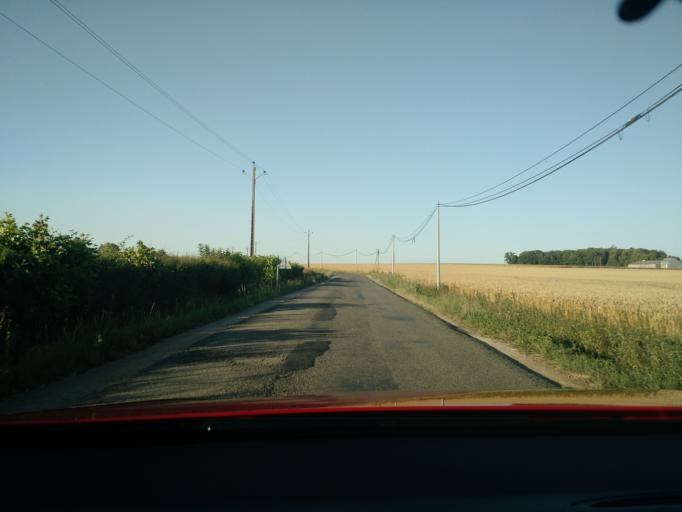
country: FR
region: Centre
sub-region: Departement de l'Indre
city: Montierchaume
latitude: 46.8808
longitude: 1.7267
